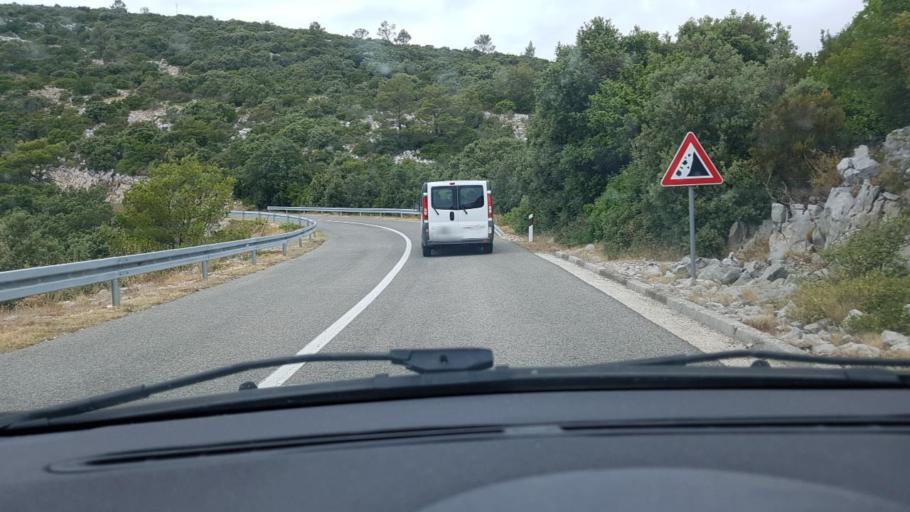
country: HR
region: Dubrovacko-Neretvanska
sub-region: Grad Korcula
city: Zrnovo
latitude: 42.9386
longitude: 17.0196
